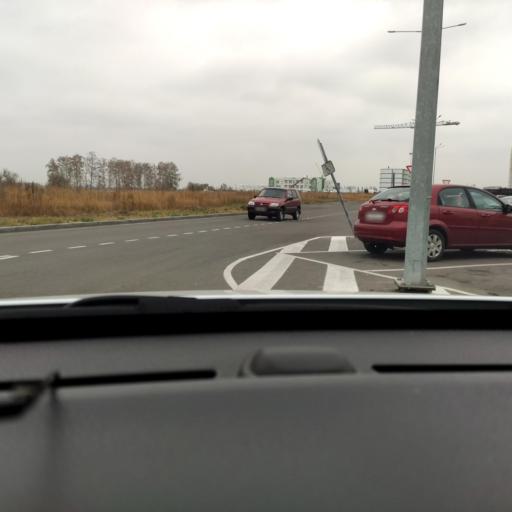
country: RU
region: Voronezj
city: Novaya Usman'
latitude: 51.6508
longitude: 39.3090
